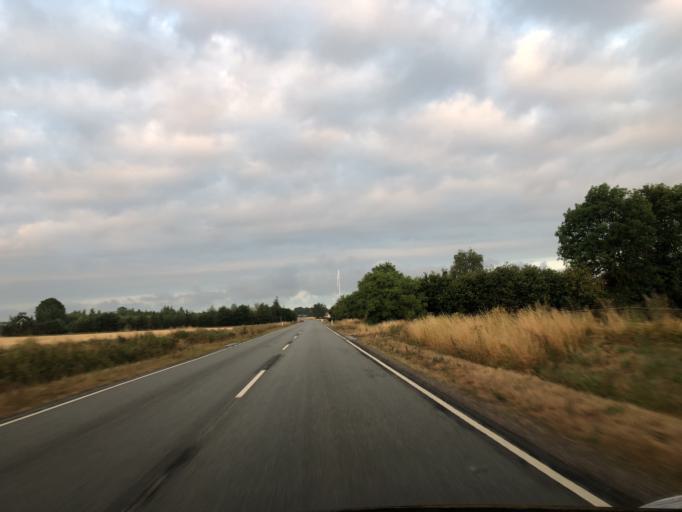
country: DK
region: Zealand
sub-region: Slagelse Kommune
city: Slagelse
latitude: 55.4440
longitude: 11.4249
